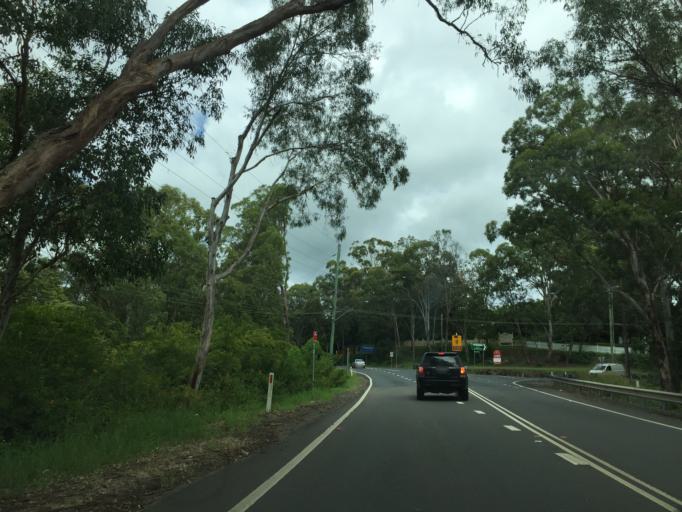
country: AU
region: New South Wales
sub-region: Hawkesbury
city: Richmond
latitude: -33.5483
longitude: 150.6766
